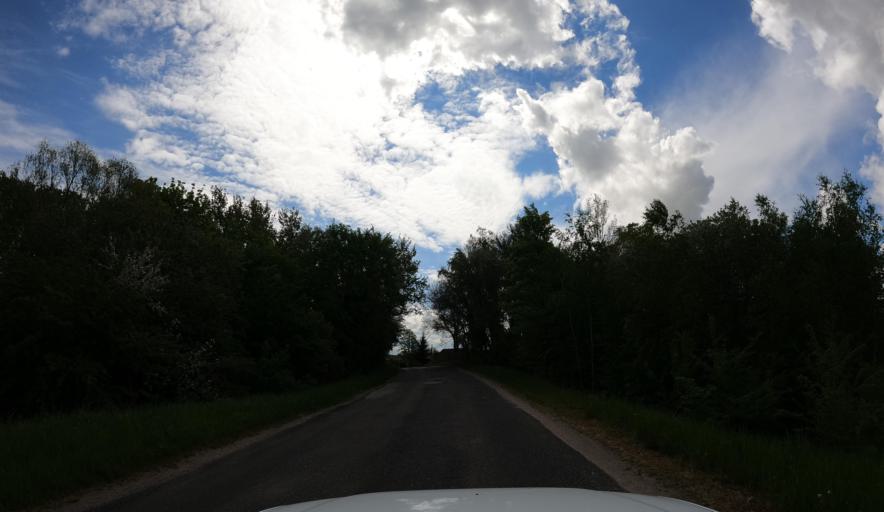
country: PL
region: West Pomeranian Voivodeship
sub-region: Powiat kamienski
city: Wolin
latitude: 53.8691
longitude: 14.6483
